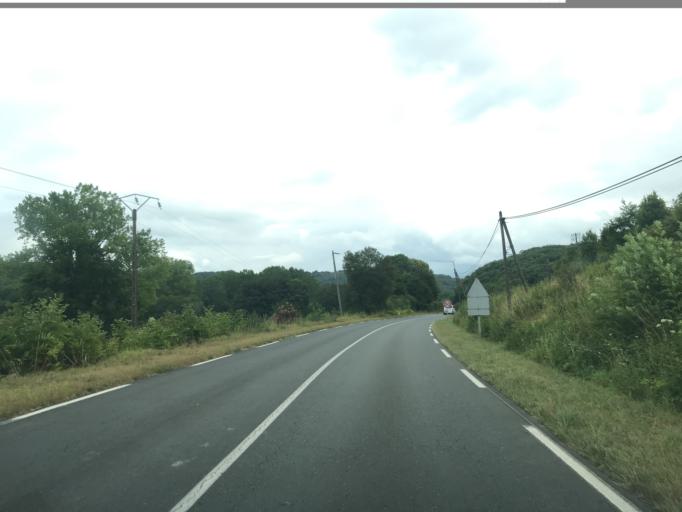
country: FR
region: Aquitaine
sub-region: Departement de la Dordogne
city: Le Bugue
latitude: 44.9603
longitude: 0.9861
